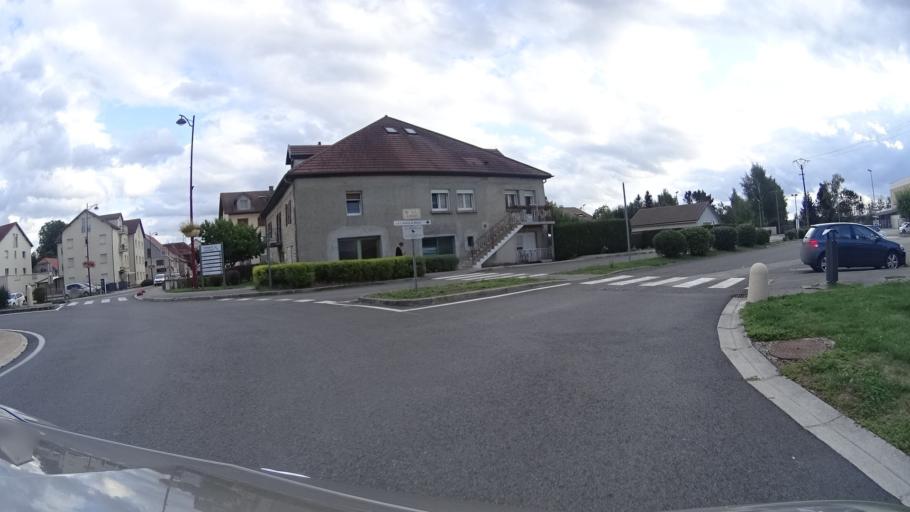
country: FR
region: Franche-Comte
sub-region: Departement du Doubs
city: Saone
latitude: 47.2277
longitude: 6.1142
